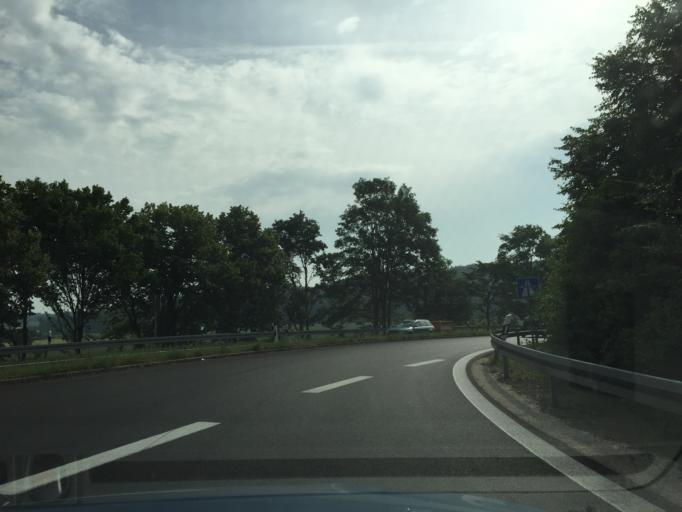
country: DE
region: Bavaria
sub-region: Swabia
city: Senden
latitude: 48.3374
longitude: 10.0349
